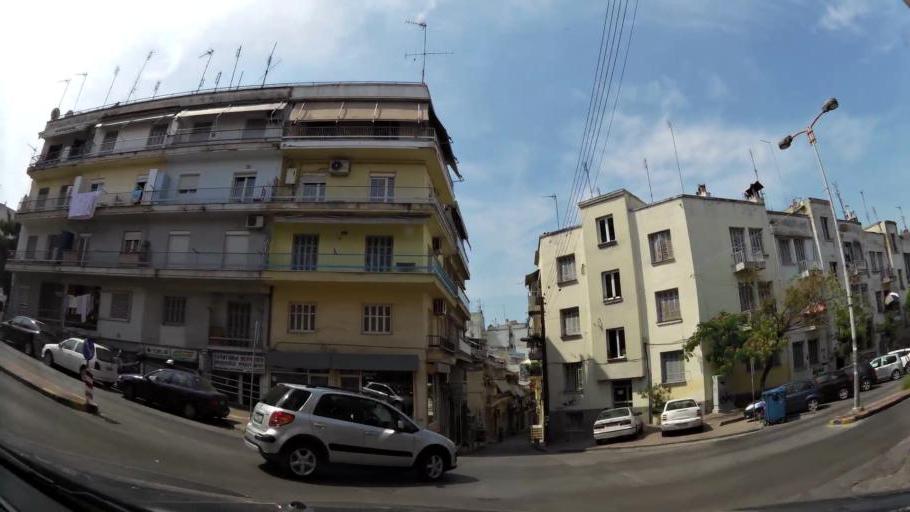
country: GR
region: Central Macedonia
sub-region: Nomos Thessalonikis
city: Sykies
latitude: 40.6421
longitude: 22.9456
